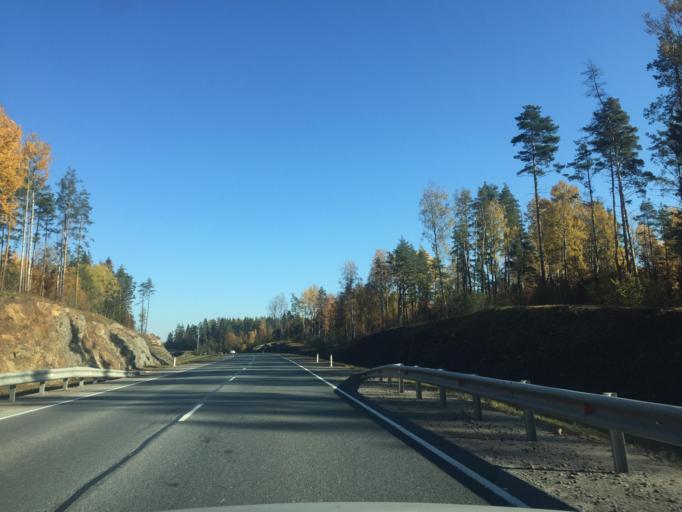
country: RU
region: Leningrad
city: Kuznechnoye
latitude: 61.2945
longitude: 29.7780
